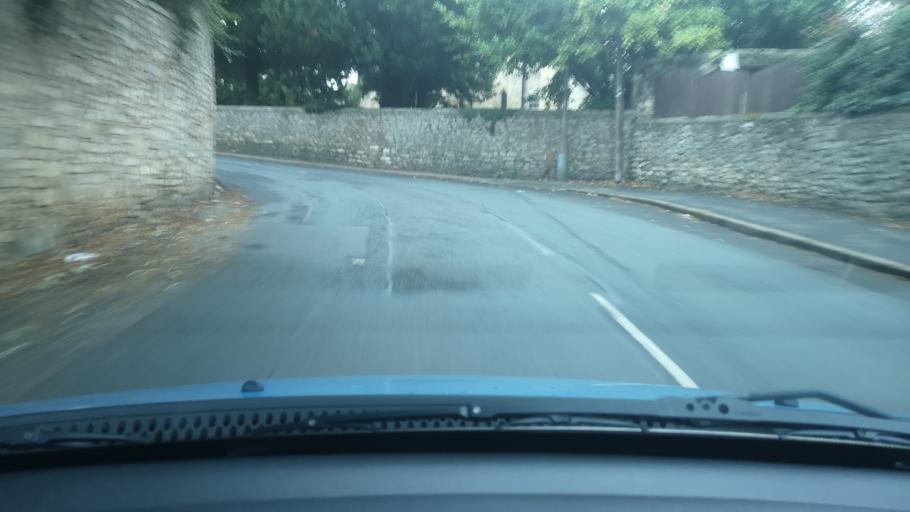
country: GB
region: England
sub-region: Doncaster
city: Campsall
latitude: 53.6200
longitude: -1.1787
